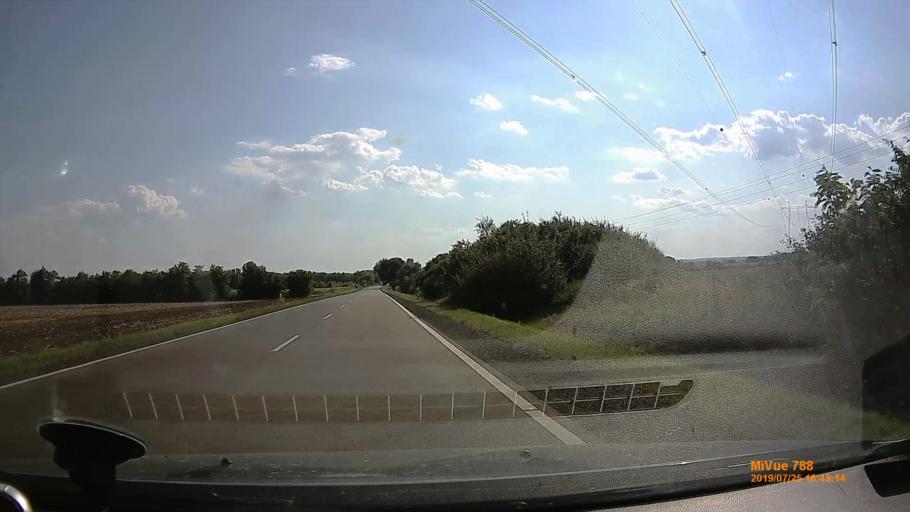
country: HU
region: Heves
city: Hort
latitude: 47.7028
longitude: 19.8164
